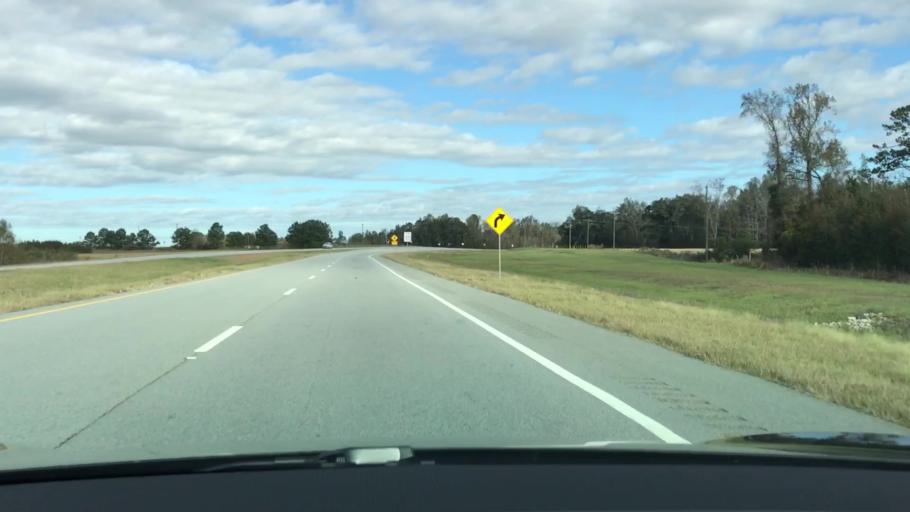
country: US
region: Georgia
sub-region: Jefferson County
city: Wadley
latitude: 32.8149
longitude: -82.4043
